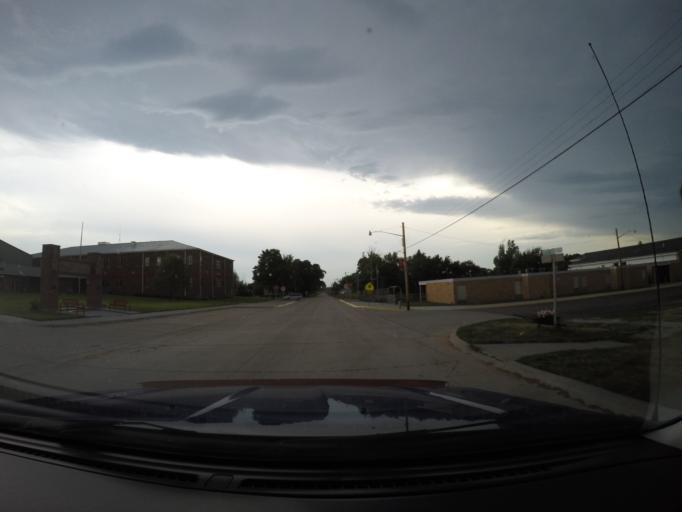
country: US
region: Nebraska
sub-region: Buffalo County
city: Kearney
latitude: 40.8385
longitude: -99.2661
